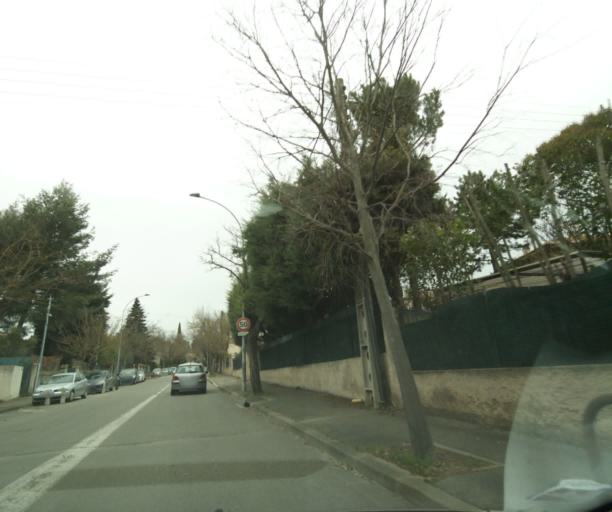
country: FR
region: Provence-Alpes-Cote d'Azur
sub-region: Departement des Bouches-du-Rhone
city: Aix-en-Provence
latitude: 43.5188
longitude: 5.4577
